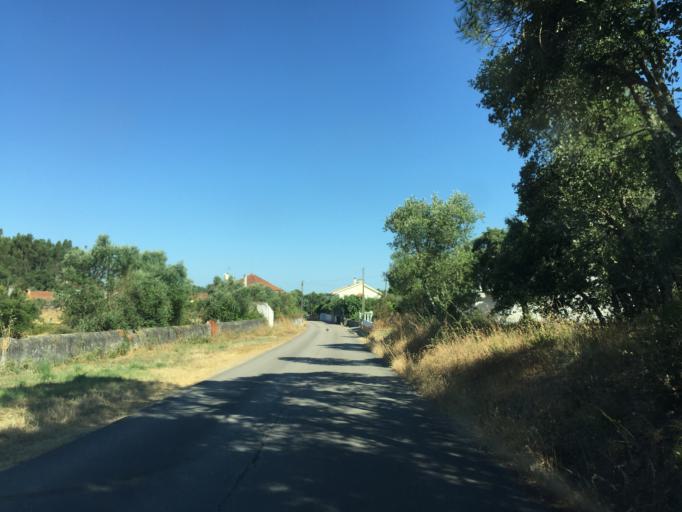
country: PT
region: Santarem
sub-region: Tomar
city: Tomar
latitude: 39.6043
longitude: -8.3287
